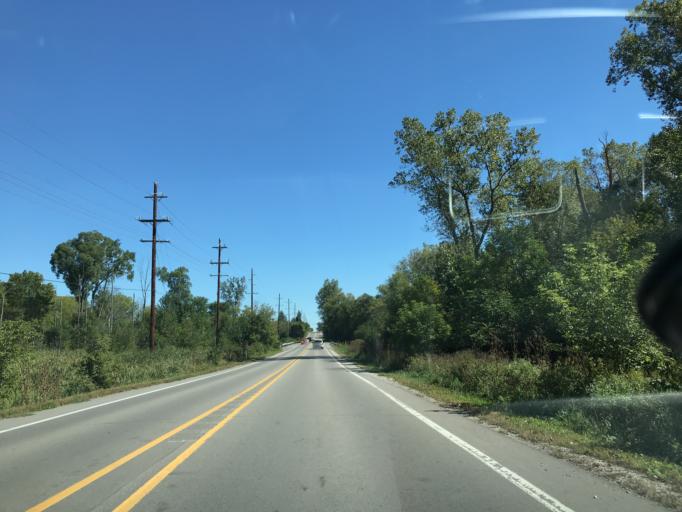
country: US
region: Michigan
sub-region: Washtenaw County
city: Ypsilanti
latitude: 42.2750
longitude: -83.6214
